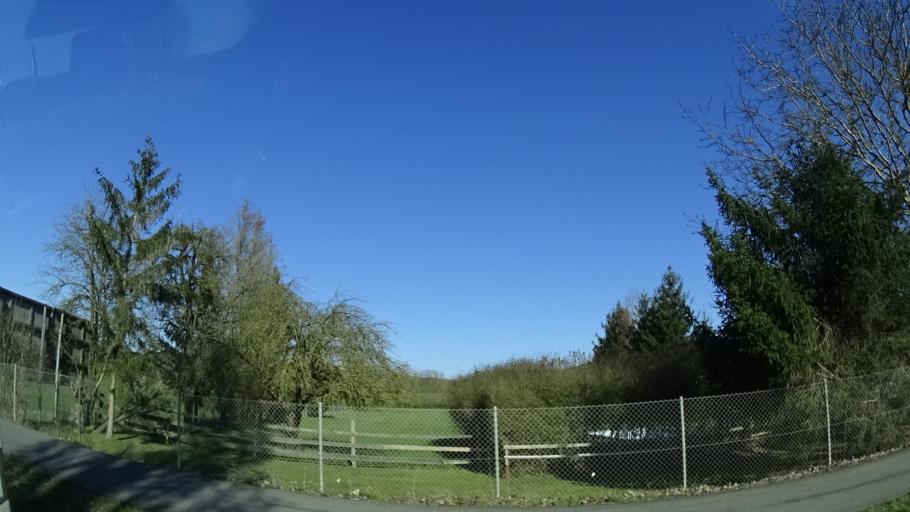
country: DE
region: Thuringia
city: Romhild
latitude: 50.4047
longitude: 10.5385
